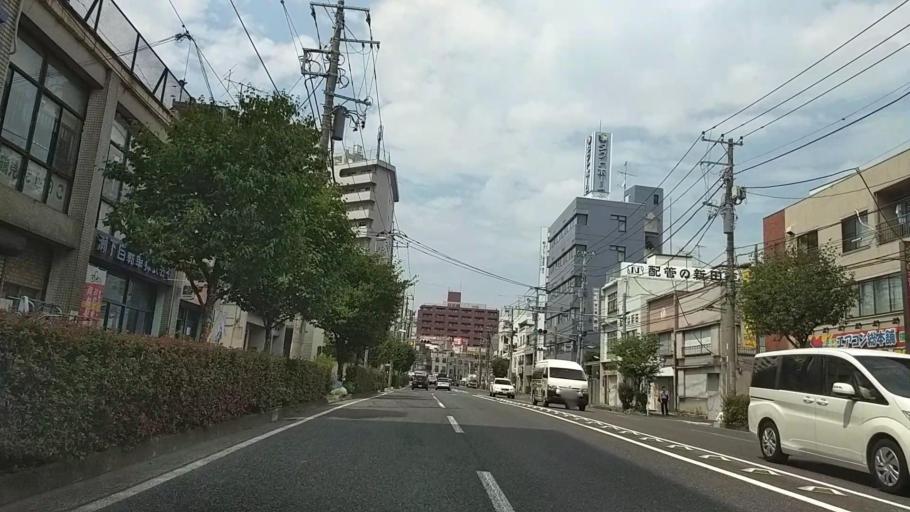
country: JP
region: Kanagawa
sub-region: Kawasaki-shi
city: Kawasaki
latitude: 35.5125
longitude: 139.6761
